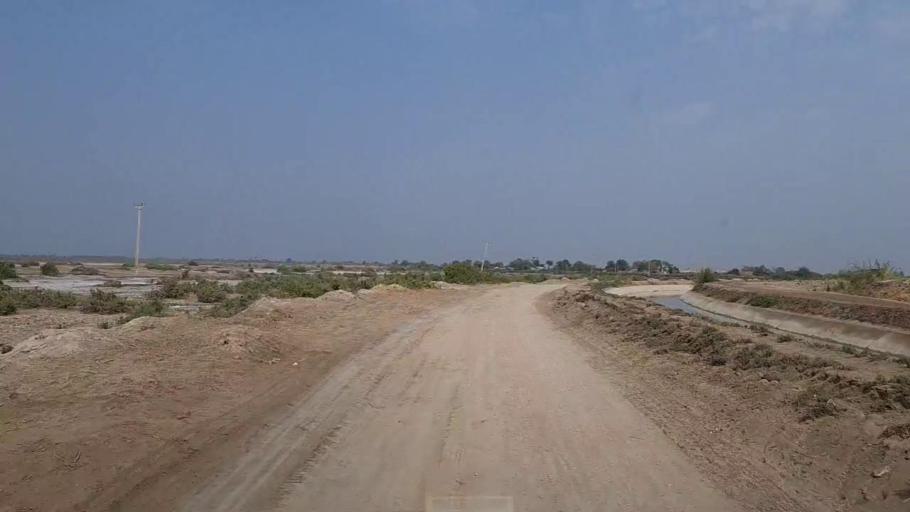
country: PK
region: Sindh
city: Mirwah Gorchani
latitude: 25.3987
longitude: 69.0753
